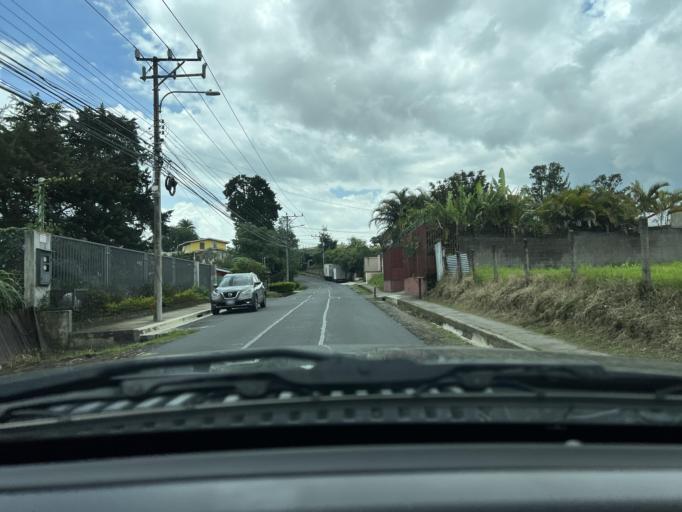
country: CR
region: San Jose
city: Granadilla
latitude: 9.9406
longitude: -84.0244
